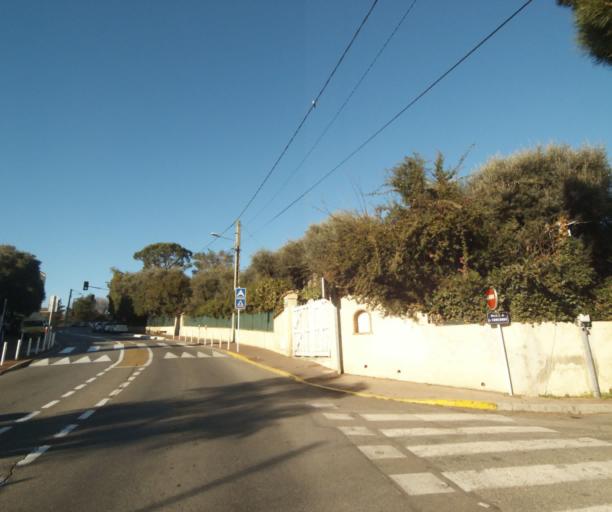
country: FR
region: Provence-Alpes-Cote d'Azur
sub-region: Departement des Alpes-Maritimes
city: Antibes
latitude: 43.5809
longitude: 7.1130
